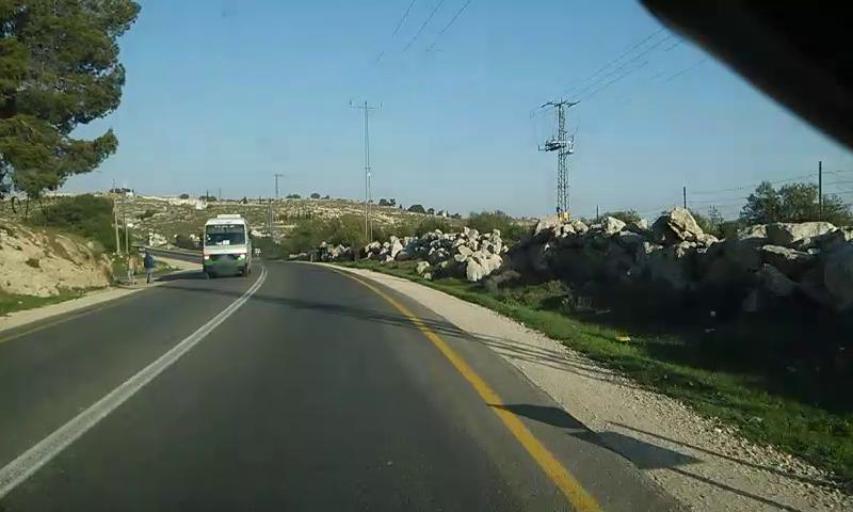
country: PS
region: West Bank
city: Jurat ash Sham`ah
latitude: 31.6471
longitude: 35.1577
